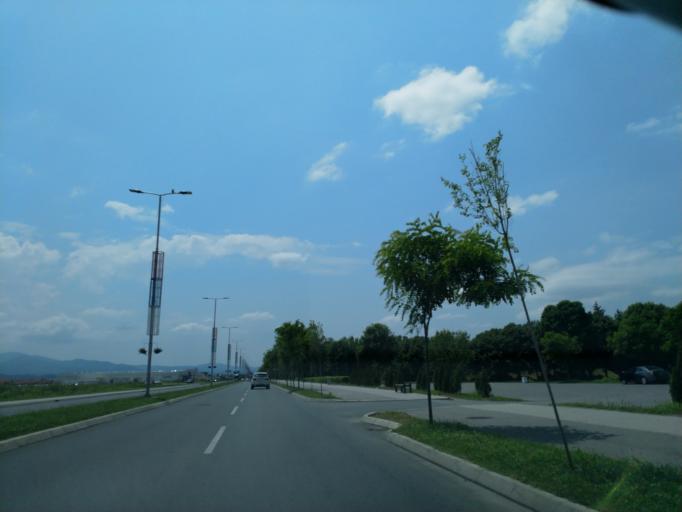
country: RS
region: Central Serbia
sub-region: Rasinski Okrug
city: Krusevac
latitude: 43.5647
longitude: 21.3353
